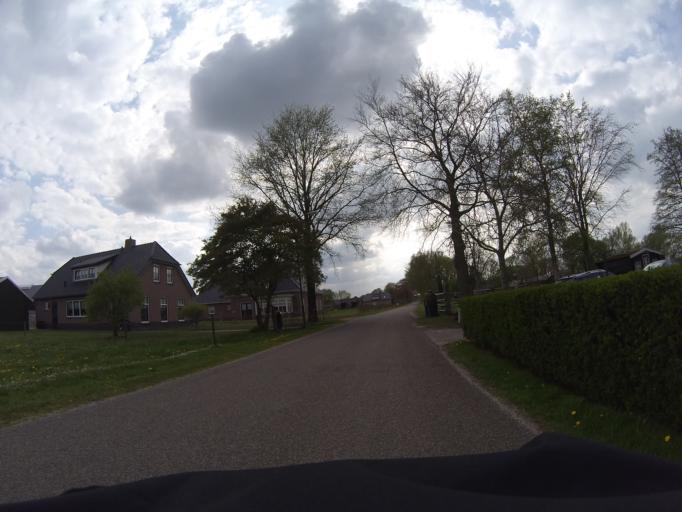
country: NL
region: Gelderland
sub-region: Gemeente Oldebroek
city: Oldebroek
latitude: 52.4501
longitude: 5.9390
